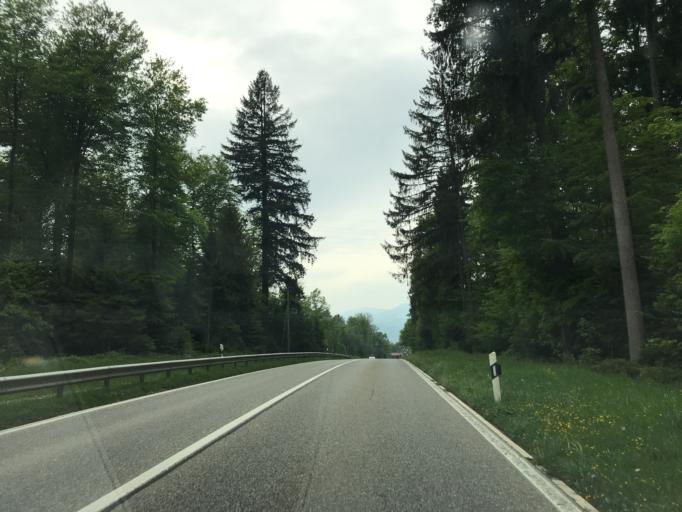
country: CH
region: Bern
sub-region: Oberaargau
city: Niederbipp
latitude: 47.2510
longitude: 7.7266
